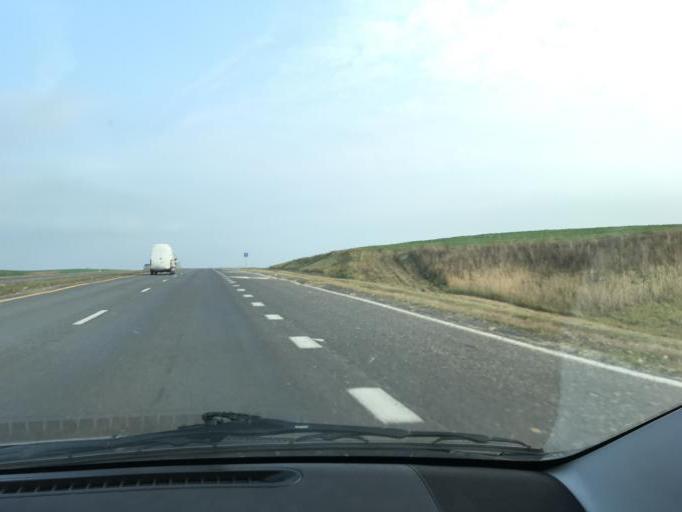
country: BY
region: Vitebsk
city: Vitebsk
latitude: 55.1538
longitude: 30.0133
